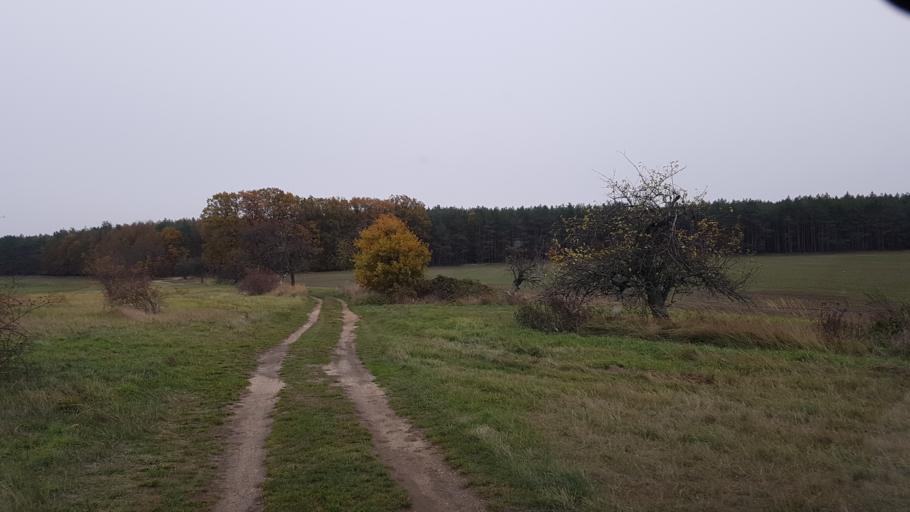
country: DE
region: Brandenburg
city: Crinitz
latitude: 51.7293
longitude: 13.7599
